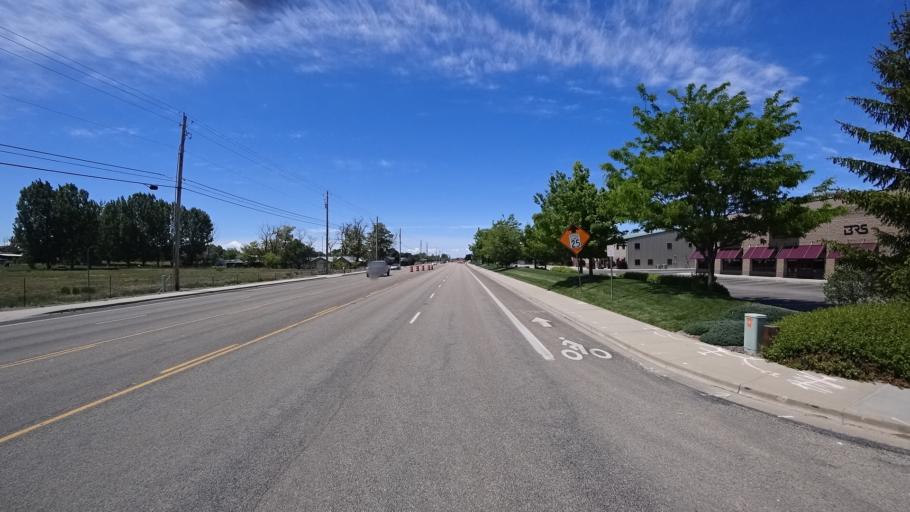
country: US
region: Idaho
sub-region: Ada County
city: Garden City
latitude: 43.5756
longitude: -116.2650
